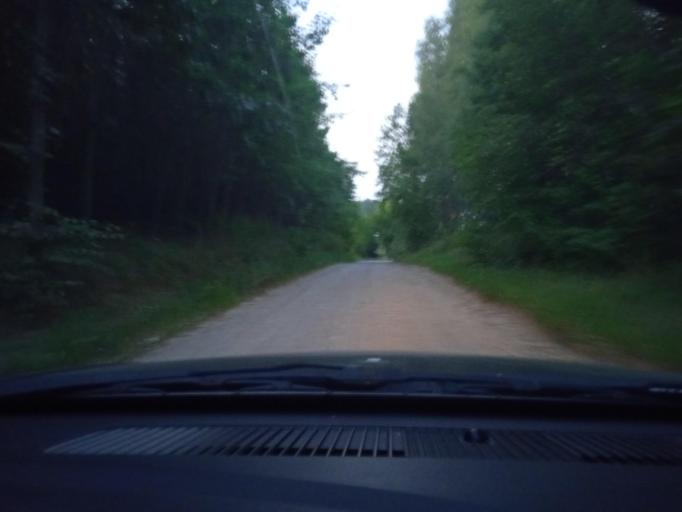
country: PL
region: Masovian Voivodeship
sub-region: Powiat nowodworski
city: Pomiechowek
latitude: 52.4891
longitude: 20.7043
